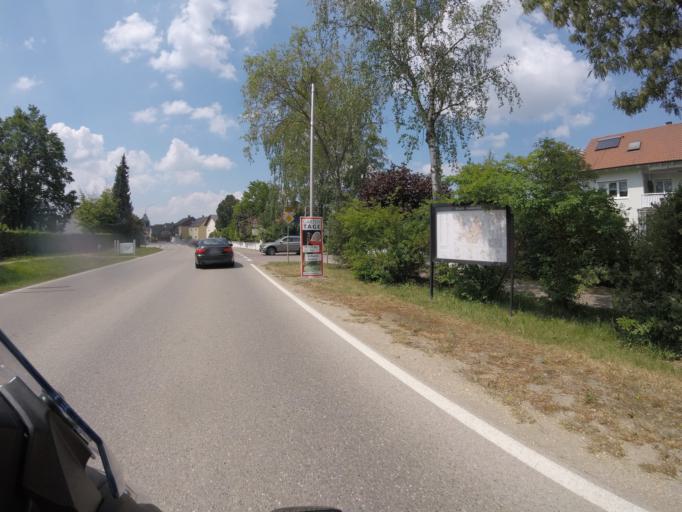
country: DE
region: Bavaria
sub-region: Upper Bavaria
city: Geisenfeld
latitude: 48.6873
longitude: 11.6224
